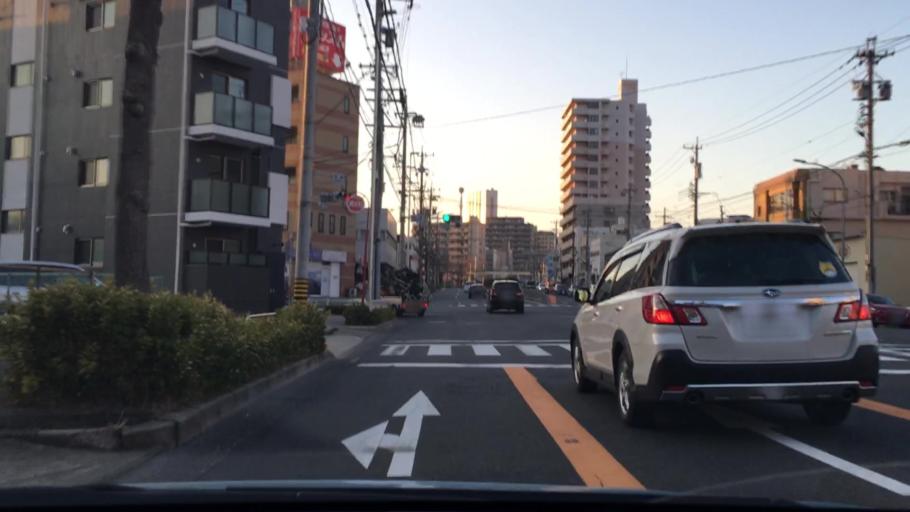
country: JP
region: Aichi
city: Nagoya-shi
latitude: 35.1340
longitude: 136.9069
